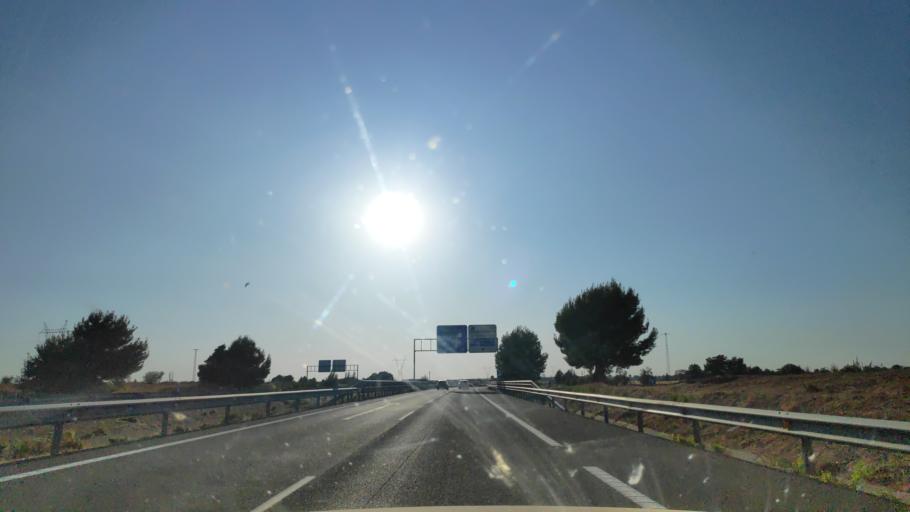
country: ES
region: Castille-La Mancha
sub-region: Provincia de Cuenca
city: Tarancon
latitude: 39.9952
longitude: -3.0096
